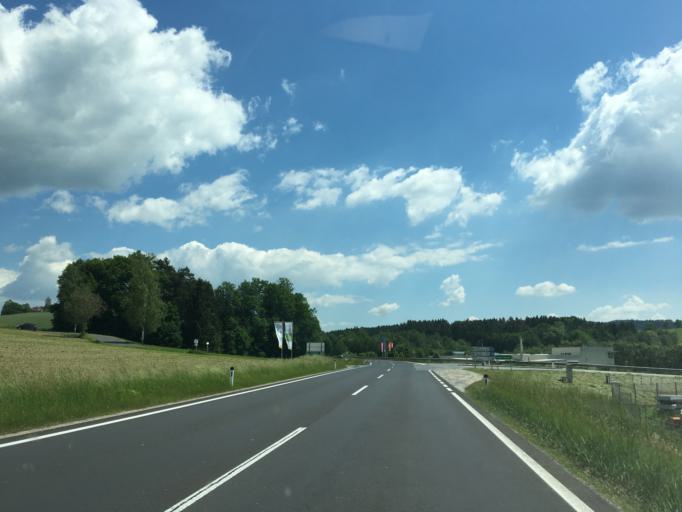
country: AT
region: Upper Austria
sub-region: Politischer Bezirk Perg
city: Perg
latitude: 48.3345
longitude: 14.5720
